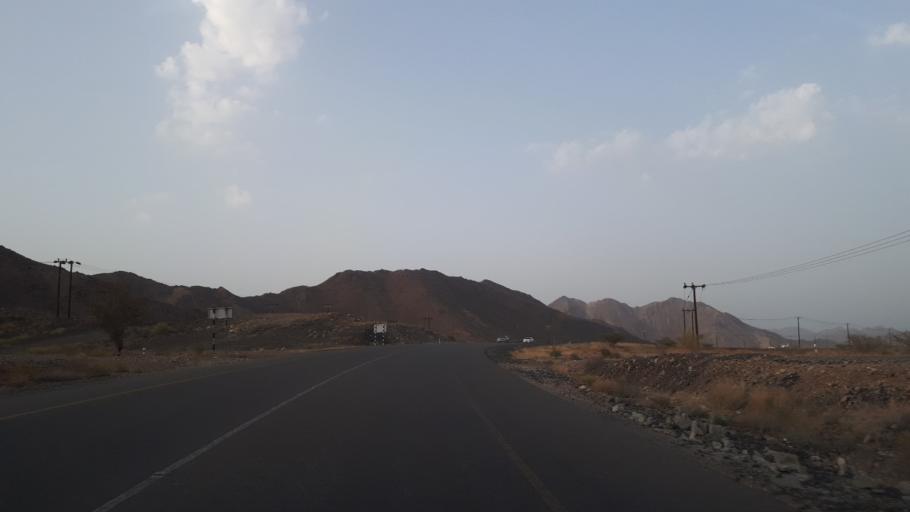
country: OM
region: Al Batinah
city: Rustaq
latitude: 23.4035
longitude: 57.2414
